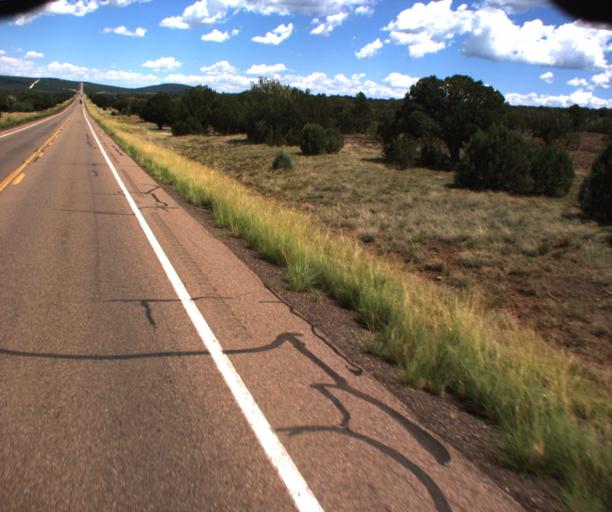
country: US
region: Arizona
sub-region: Navajo County
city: White Mountain Lake
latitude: 34.2798
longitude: -109.8721
